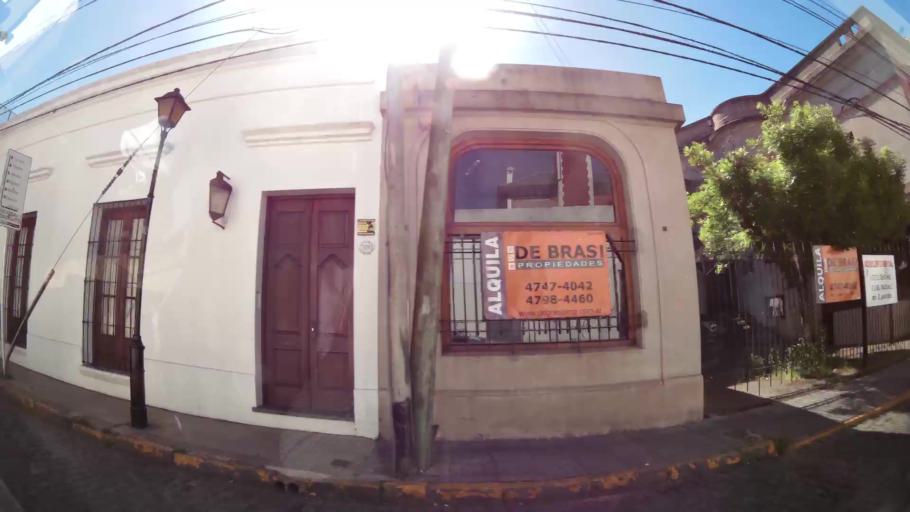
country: AR
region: Buenos Aires
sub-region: Partido de San Isidro
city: San Isidro
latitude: -34.4671
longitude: -58.5105
